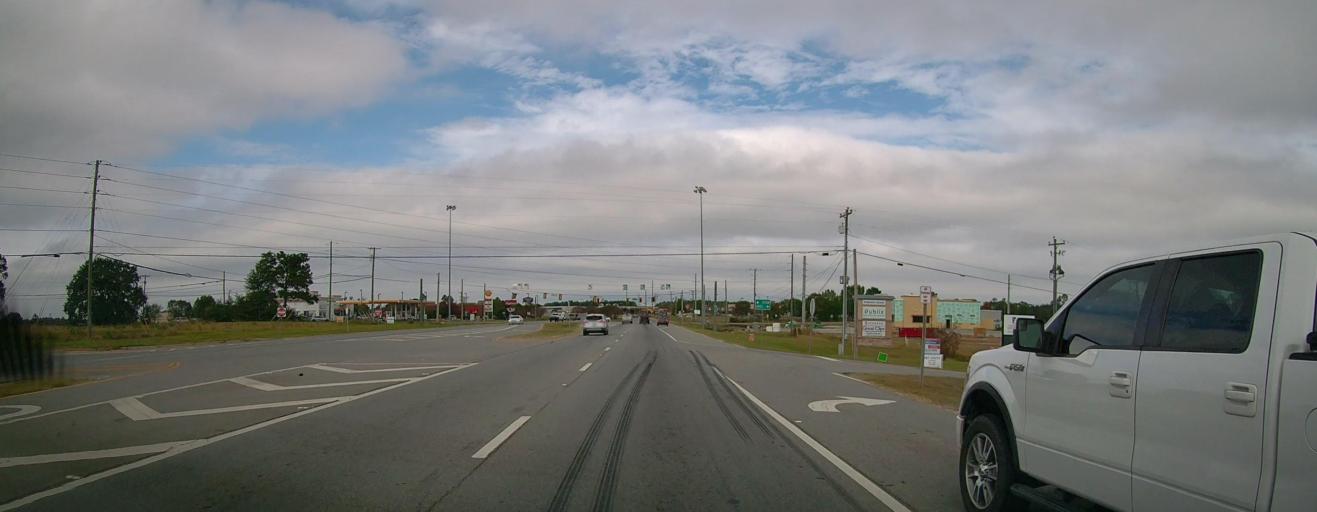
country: US
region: Georgia
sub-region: Colquitt County
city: Moultrie
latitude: 31.1849
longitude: -83.7615
